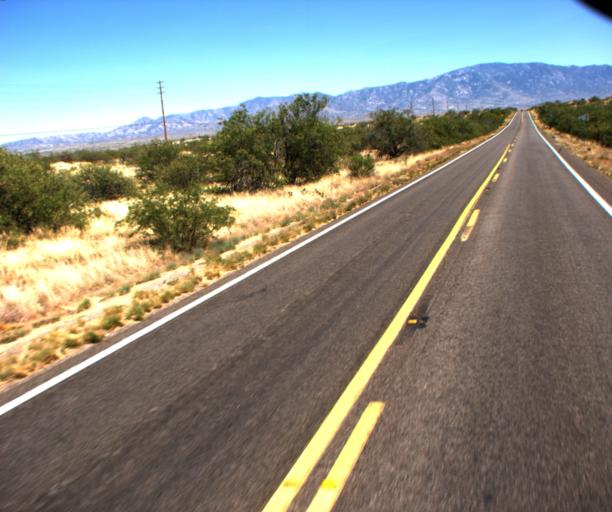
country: US
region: Arizona
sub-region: Pima County
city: Catalina
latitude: 32.5991
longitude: -110.9781
